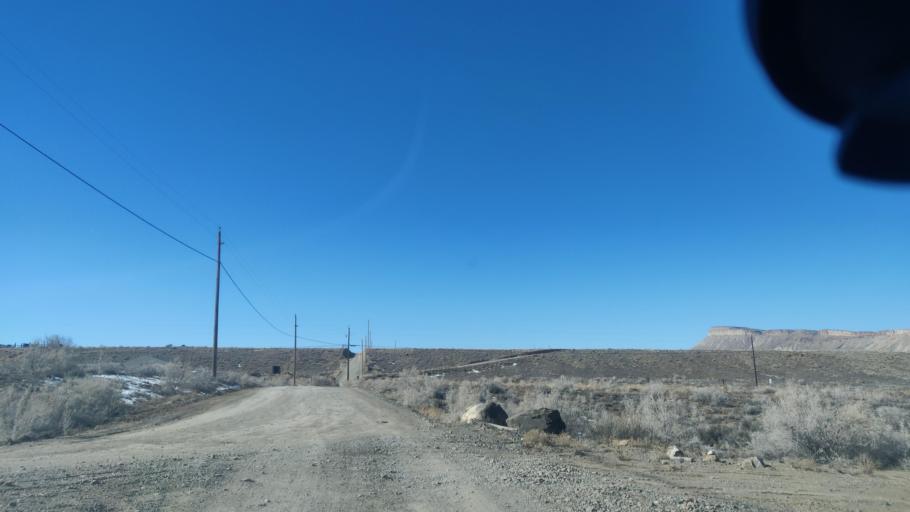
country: US
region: Colorado
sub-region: Mesa County
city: Palisade
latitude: 39.0916
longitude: -108.3282
